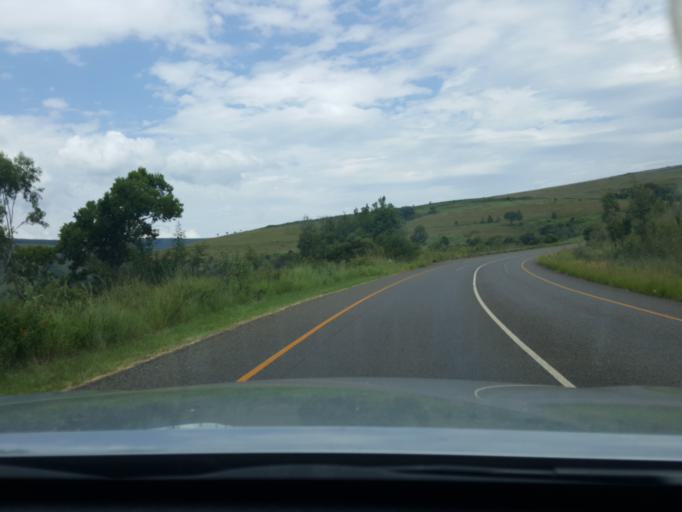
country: ZA
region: Mpumalanga
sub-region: Ehlanzeni District
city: Graksop
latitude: -25.1000
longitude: 30.8006
